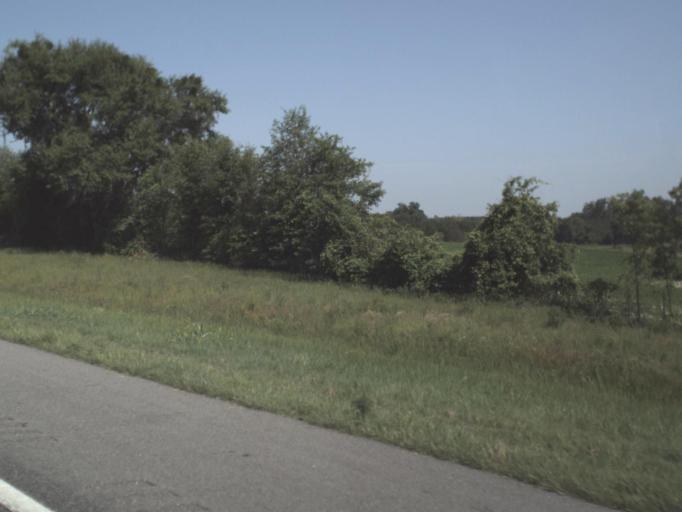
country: US
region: Florida
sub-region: Suwannee County
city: Live Oak
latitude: 30.3509
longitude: -83.0161
